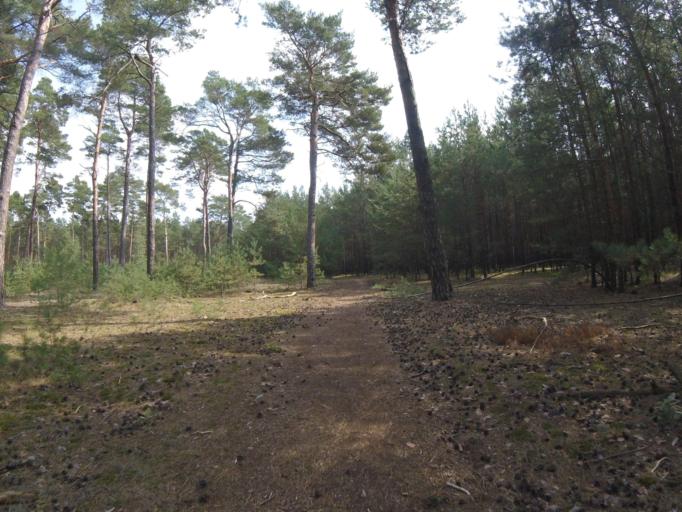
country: DE
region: Brandenburg
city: Bestensee
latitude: 52.2718
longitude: 13.6632
